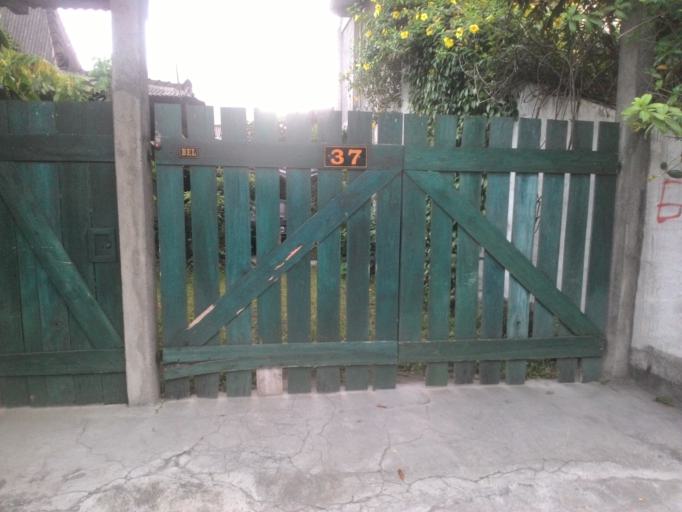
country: ID
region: Daerah Istimewa Yogyakarta
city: Yogyakarta
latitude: -7.7934
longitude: 110.3595
